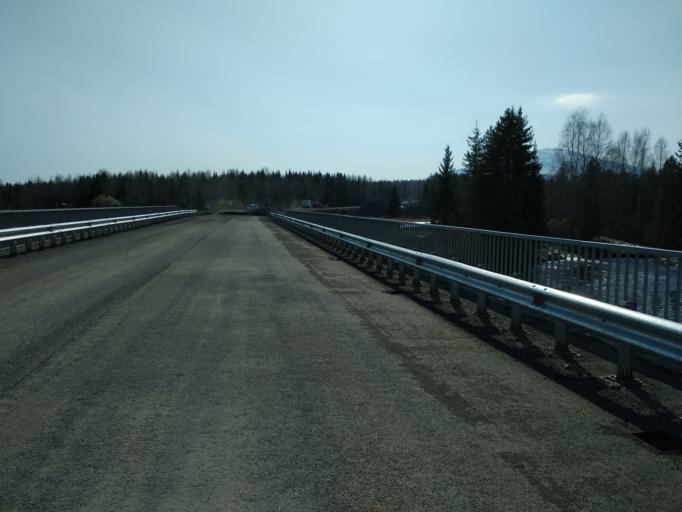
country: RU
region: Sverdlovsk
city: Karpinsk
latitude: 59.5288
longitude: 59.2607
